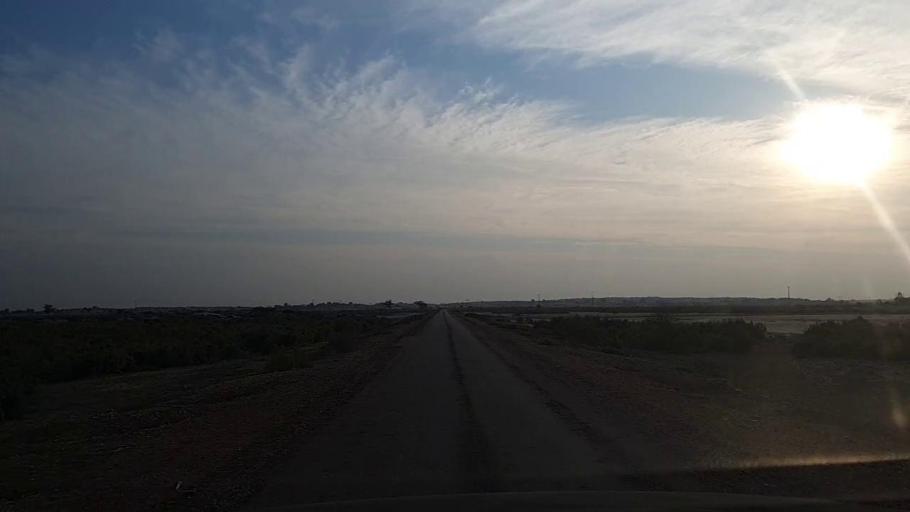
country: PK
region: Sindh
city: Jam Sahib
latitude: 26.4045
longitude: 68.5072
